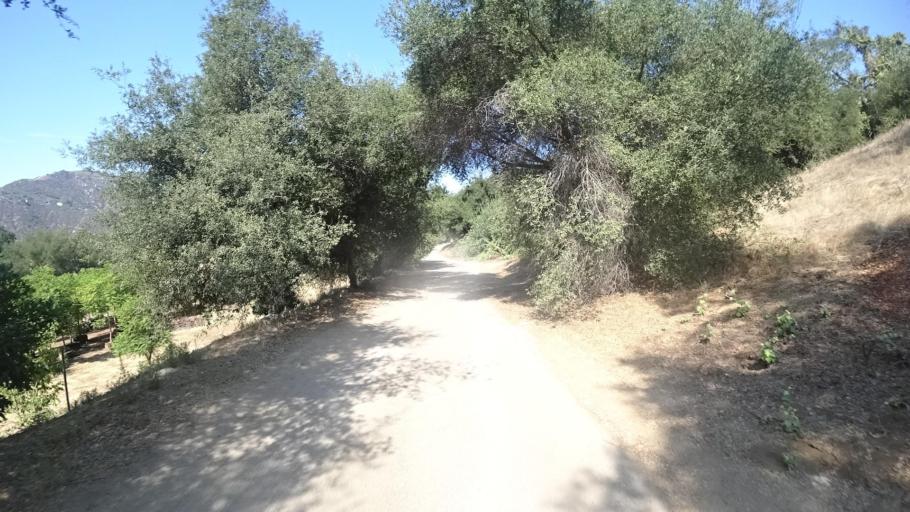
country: US
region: California
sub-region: San Diego County
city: Valley Center
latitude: 33.3417
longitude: -117.0085
